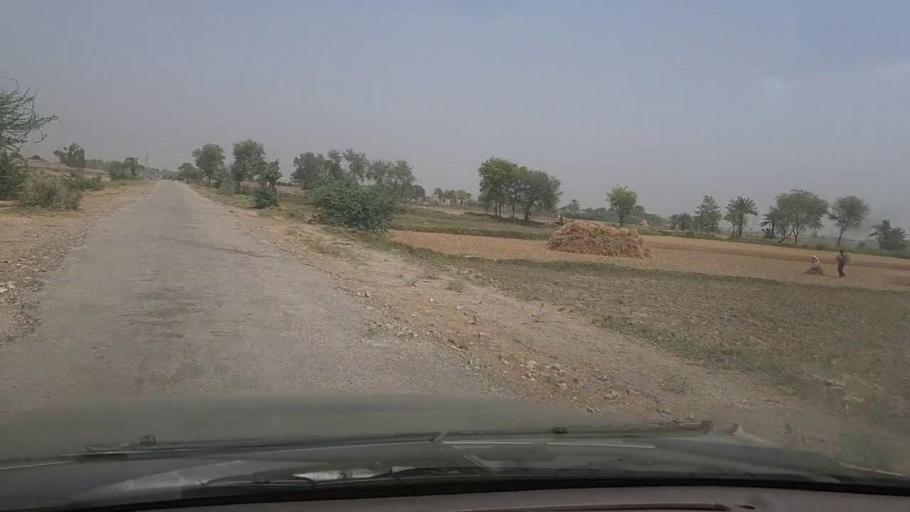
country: PK
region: Sindh
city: Madeji
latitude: 27.8220
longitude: 68.3959
